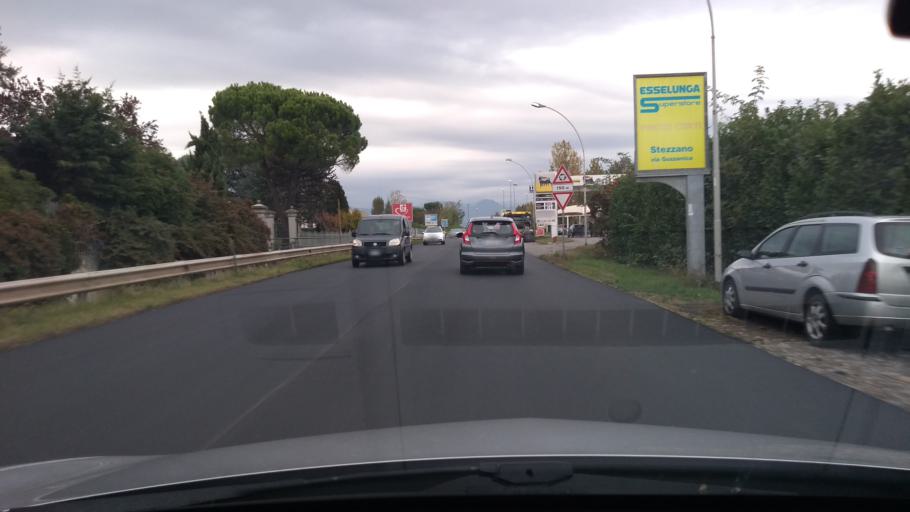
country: IT
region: Lombardy
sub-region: Provincia di Bergamo
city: Verdello
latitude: 45.6146
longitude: 9.6318
